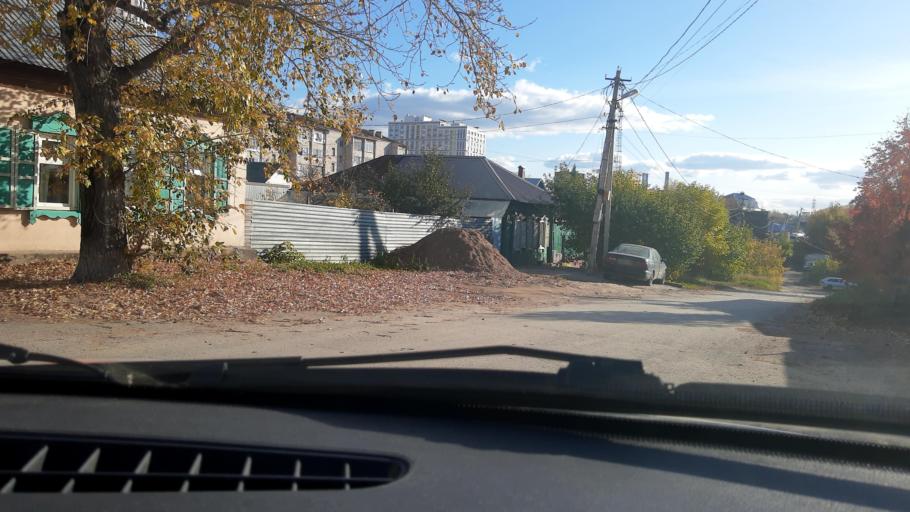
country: RU
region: Bashkortostan
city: Ufa
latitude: 54.7323
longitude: 55.9248
